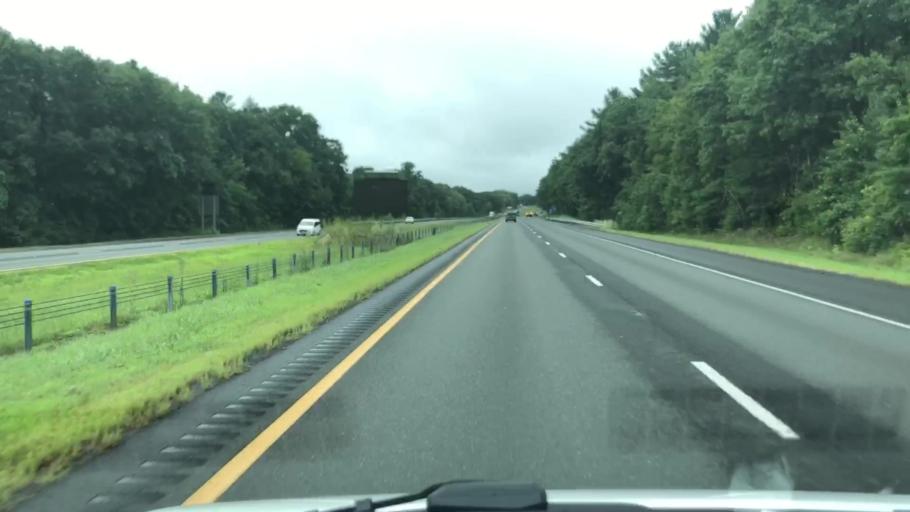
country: US
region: Massachusetts
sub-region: Hampden County
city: Holyoke
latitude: 42.2396
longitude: -72.6308
